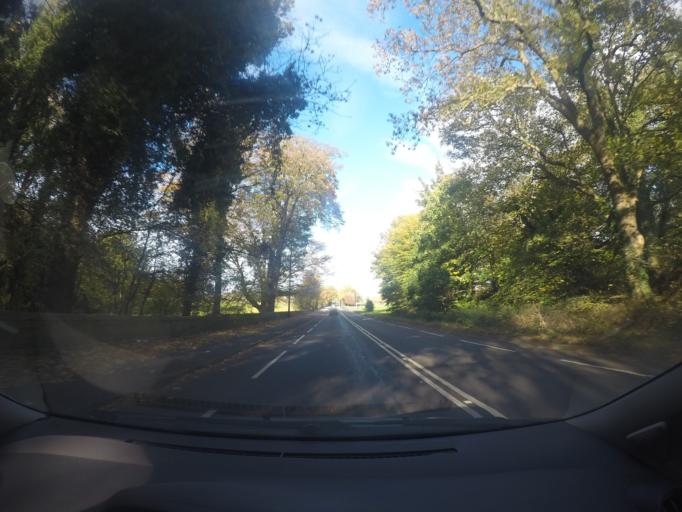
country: GB
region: England
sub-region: City and Borough of Leeds
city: Shadwell
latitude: 53.8310
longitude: -1.4758
